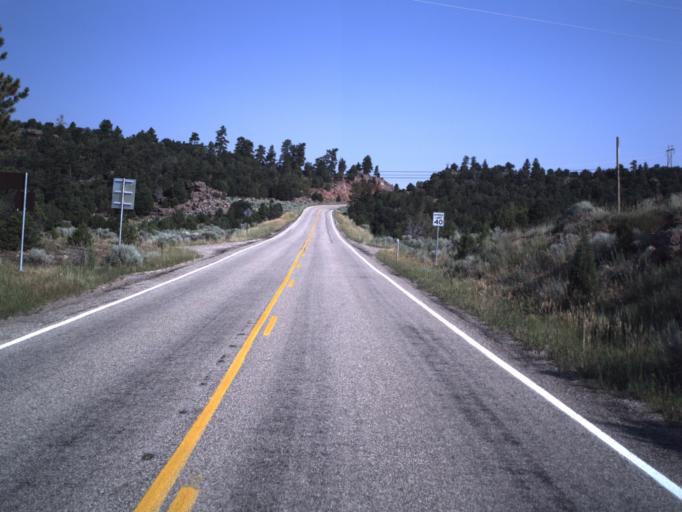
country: US
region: Utah
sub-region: Daggett County
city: Manila
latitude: 40.9134
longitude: -109.4122
